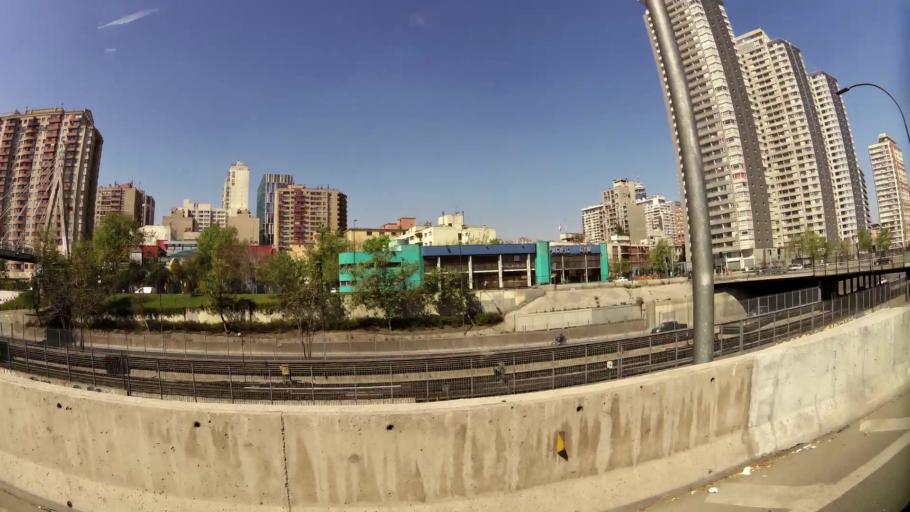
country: CL
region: Santiago Metropolitan
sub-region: Provincia de Santiago
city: Santiago
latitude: -33.4410
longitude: -70.6602
